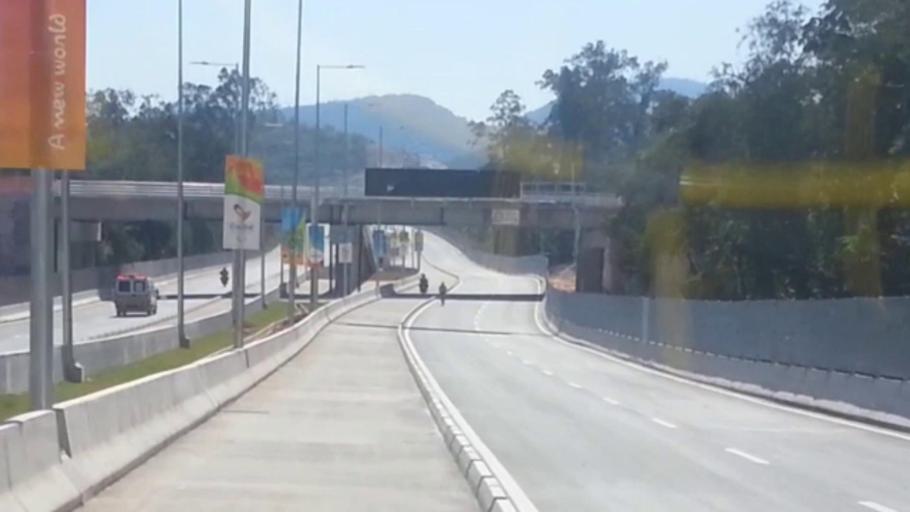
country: BR
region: Rio de Janeiro
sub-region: Nilopolis
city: Nilopolis
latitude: -22.9438
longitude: -43.3943
